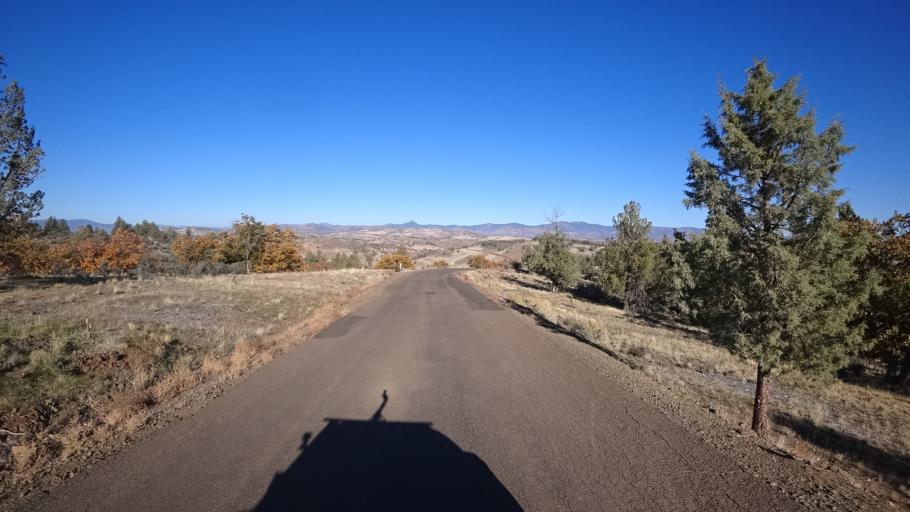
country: US
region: California
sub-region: Siskiyou County
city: Montague
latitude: 41.9092
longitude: -122.4365
